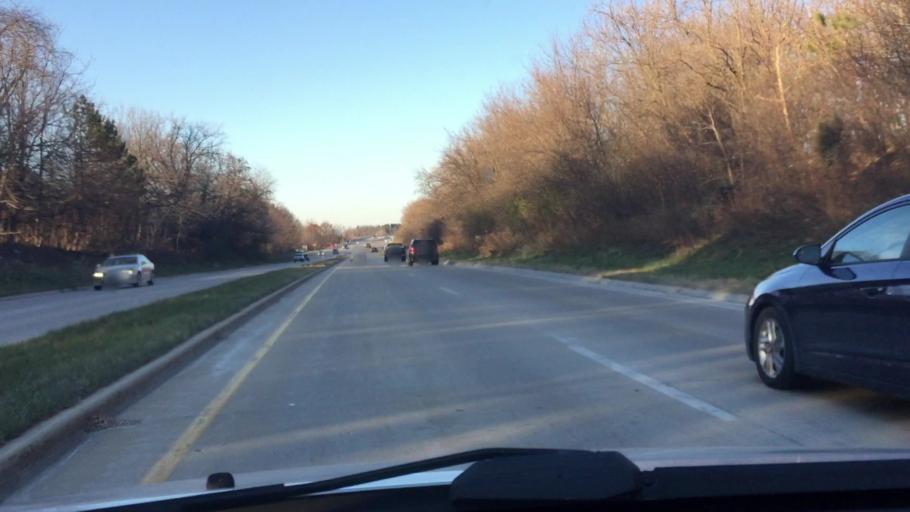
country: US
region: Wisconsin
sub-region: Waukesha County
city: Oconomowoc
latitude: 43.1015
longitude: -88.4804
